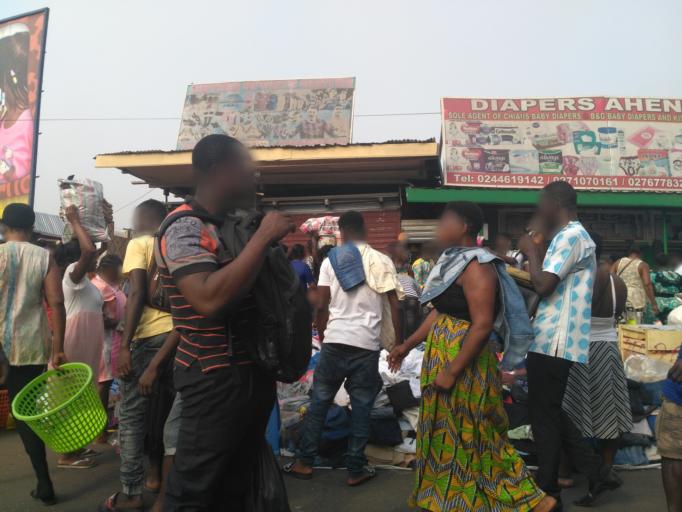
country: GH
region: Greater Accra
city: Accra
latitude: 5.5487
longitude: -0.2104
